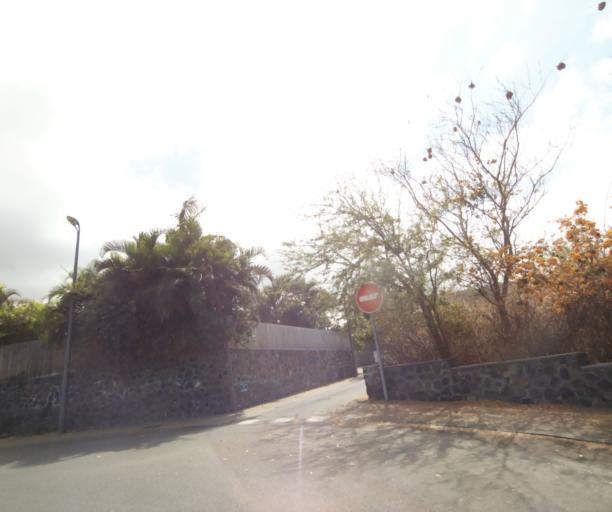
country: RE
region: Reunion
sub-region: Reunion
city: Trois-Bassins
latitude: -21.0871
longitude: 55.2391
